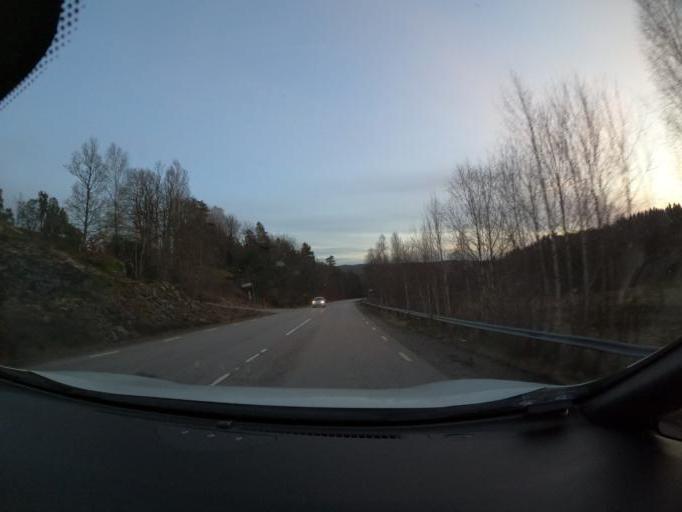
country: SE
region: Vaestra Goetaland
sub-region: Harryda Kommun
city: Molnlycke
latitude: 57.6082
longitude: 12.1791
